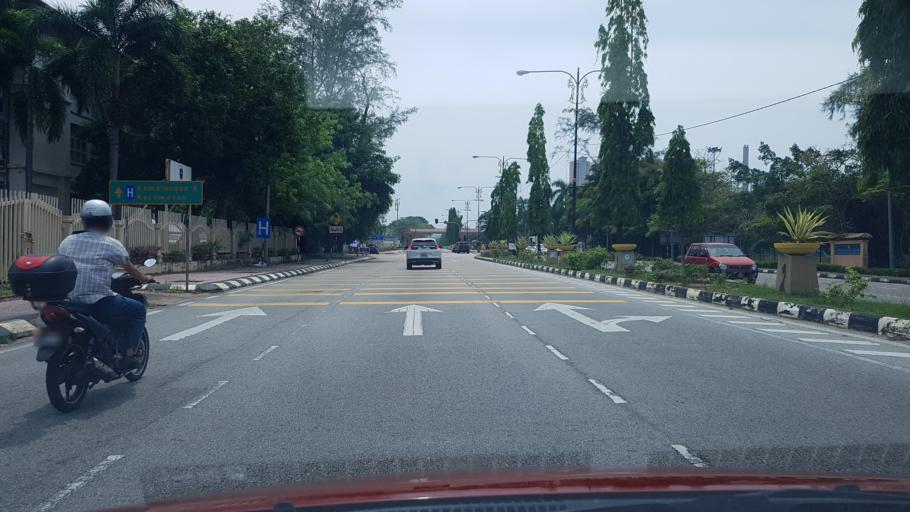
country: MY
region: Terengganu
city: Kuala Terengganu
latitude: 5.3226
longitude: 103.1515
